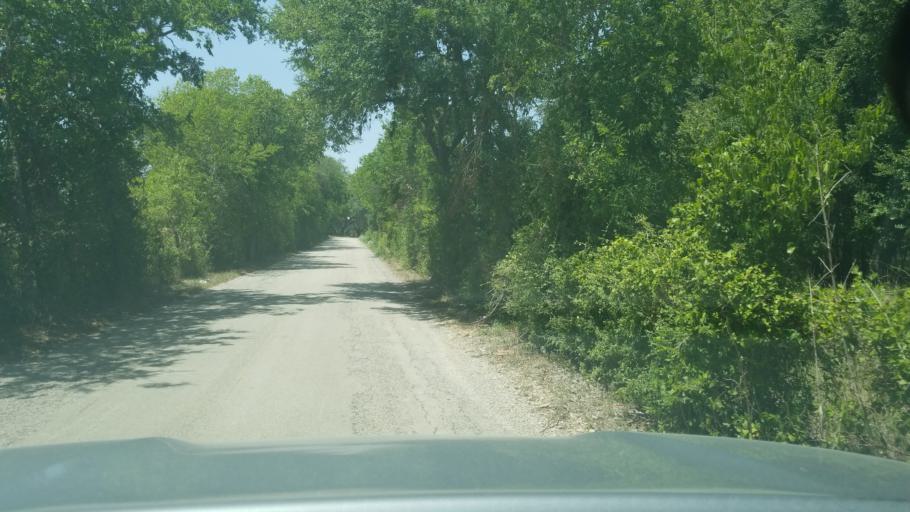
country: US
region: Texas
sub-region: Guadalupe County
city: Northcliff
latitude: 29.5935
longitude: -98.2249
